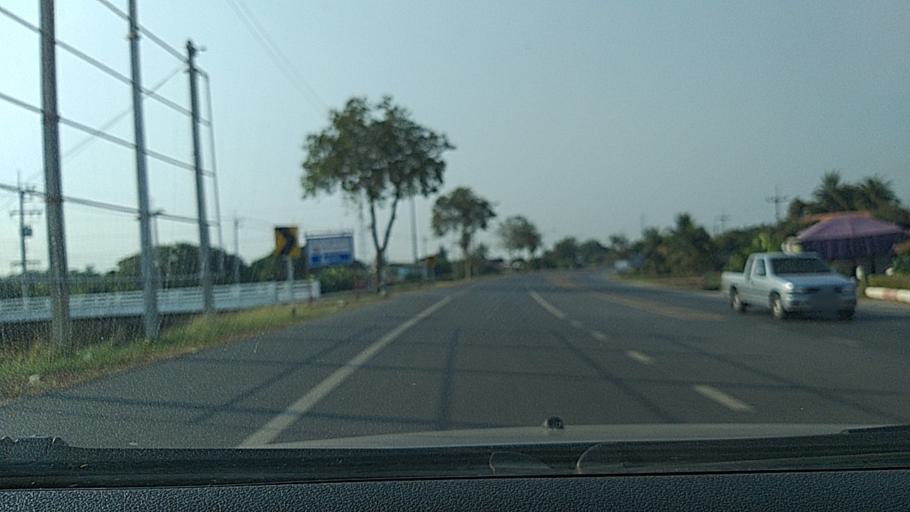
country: TH
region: Ang Thong
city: Chaiyo
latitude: 14.7157
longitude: 100.4345
